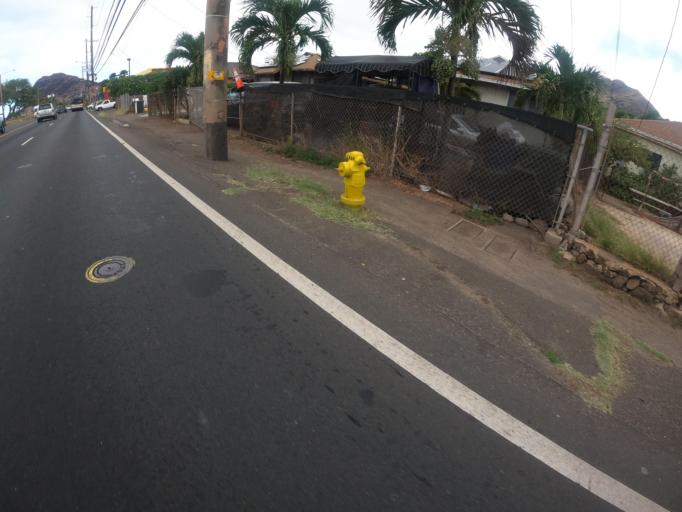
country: US
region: Hawaii
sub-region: Honolulu County
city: Nanakuli
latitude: 21.3850
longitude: -158.1493
